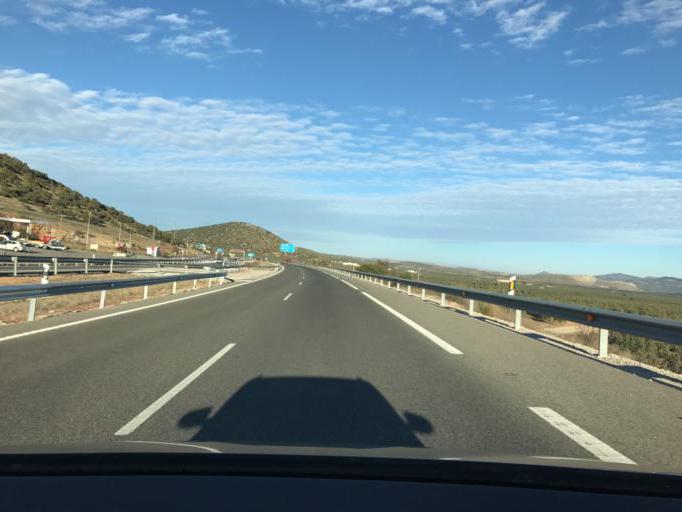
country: ES
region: Andalusia
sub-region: Provincia de Granada
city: Iznalloz
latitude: 37.3934
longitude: -3.5756
